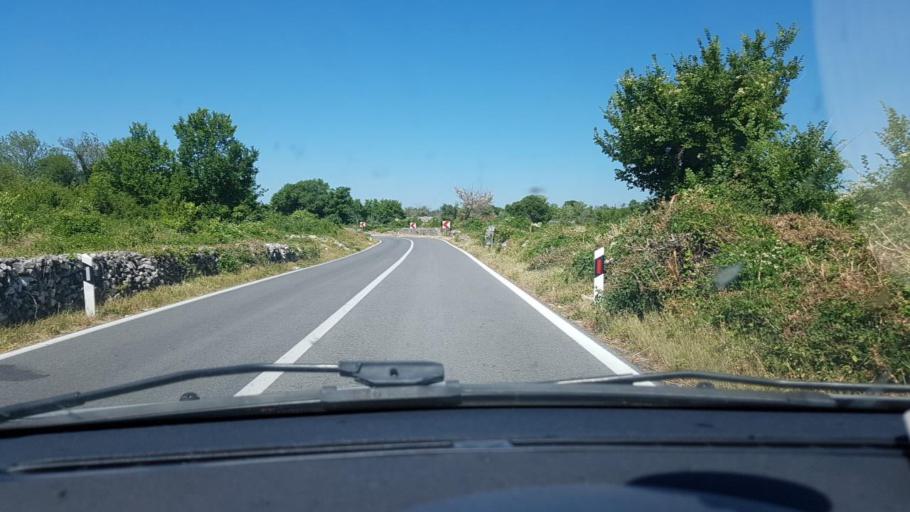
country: HR
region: Sibensko-Kniniska
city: Kistanje
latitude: 44.0185
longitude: 16.0248
